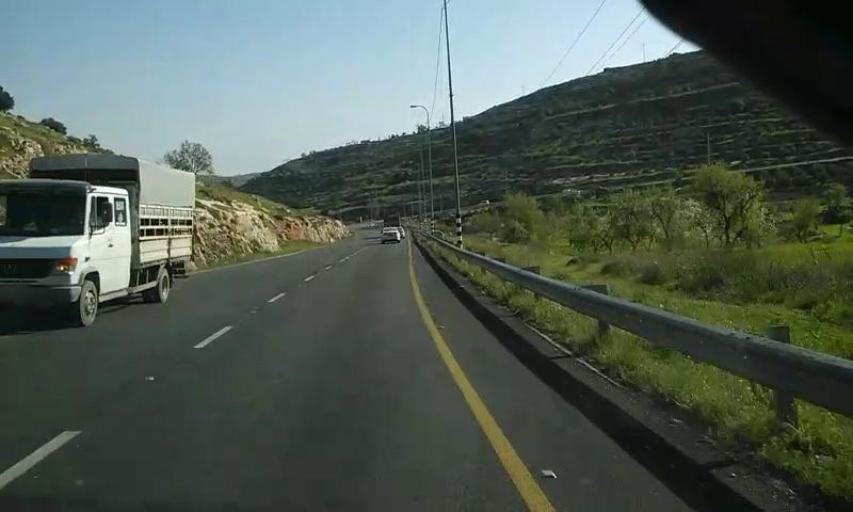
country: PS
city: Al Buq`ah
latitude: 31.5199
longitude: 35.1327
